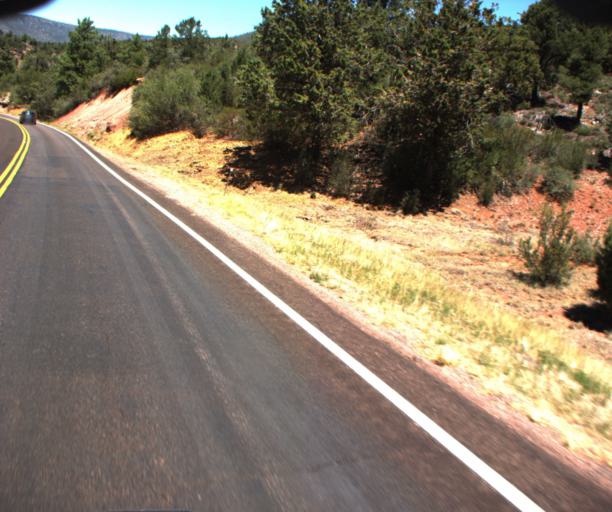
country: US
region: Arizona
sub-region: Gila County
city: Pine
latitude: 34.3607
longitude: -111.4250
